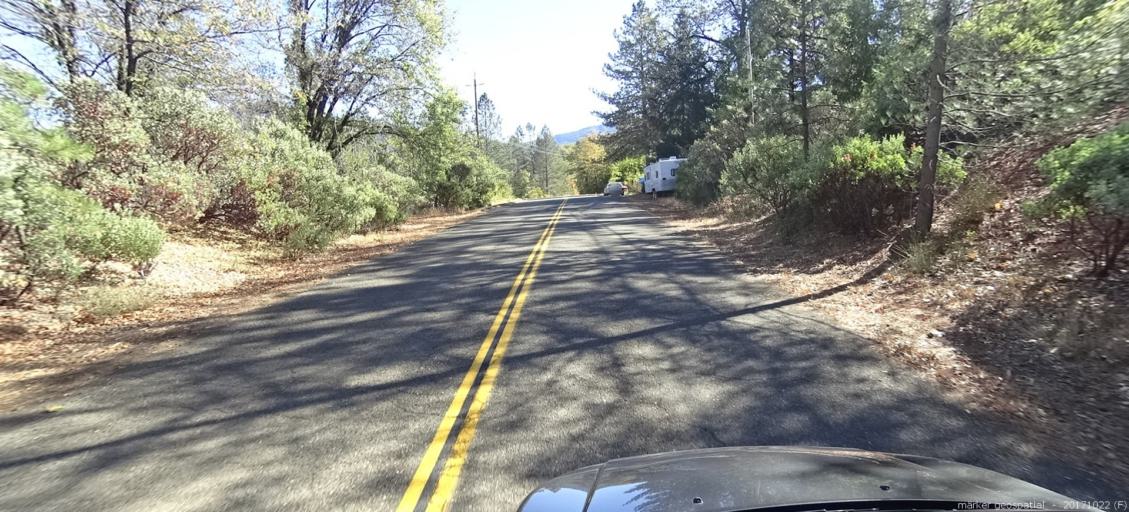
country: US
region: California
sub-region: Shasta County
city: Central Valley (historical)
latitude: 40.9171
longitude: -122.3995
